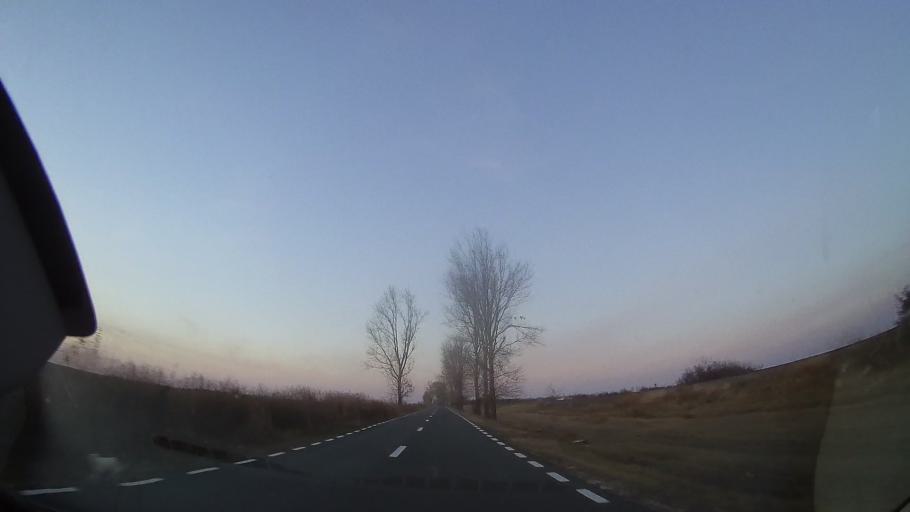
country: RO
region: Constanta
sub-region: Comuna Cobadin
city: Cobadin
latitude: 44.0410
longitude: 28.2564
